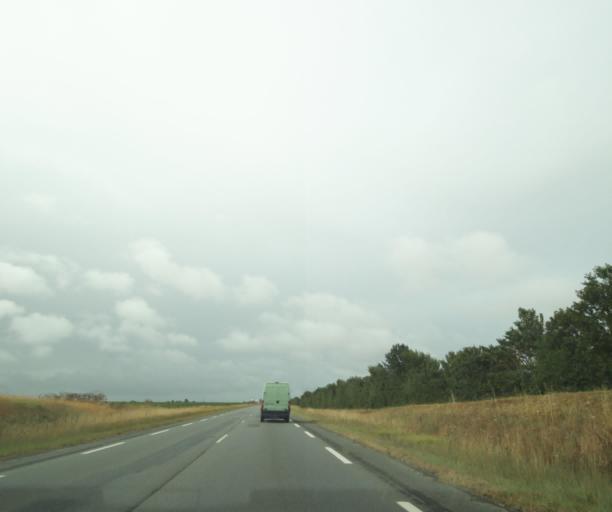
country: FR
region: Poitou-Charentes
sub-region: Departement de la Charente-Maritime
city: Lagord
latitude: 46.1993
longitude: -1.1393
